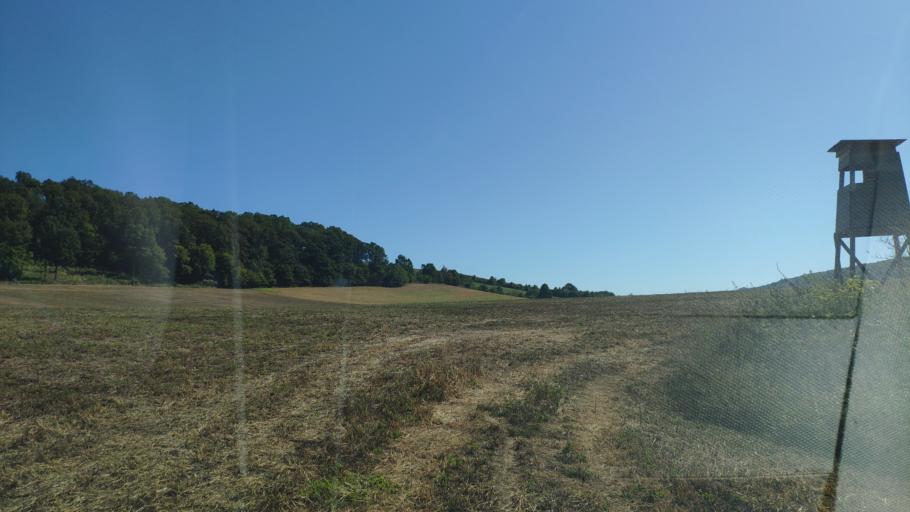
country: SK
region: Presovsky
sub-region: Okres Presov
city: Presov
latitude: 48.9683
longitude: 21.1386
